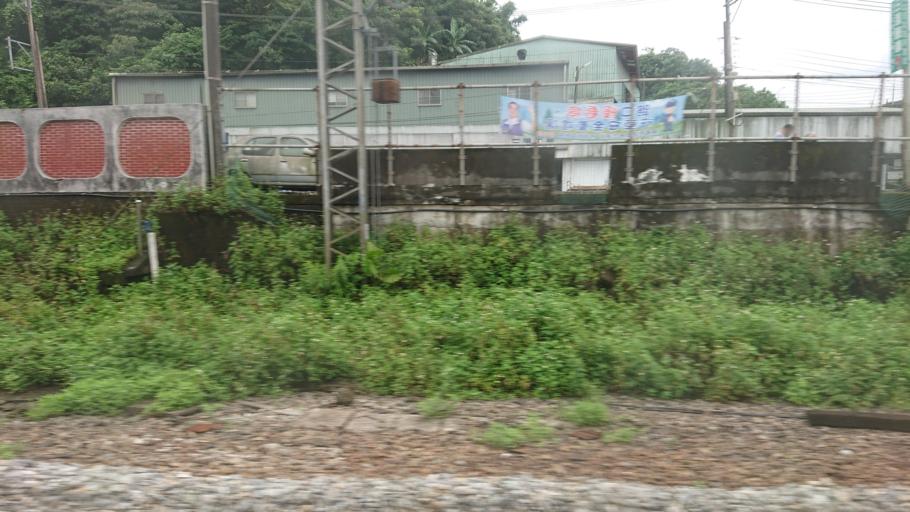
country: TW
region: Taiwan
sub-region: Keelung
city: Keelung
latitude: 25.1065
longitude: 121.7264
